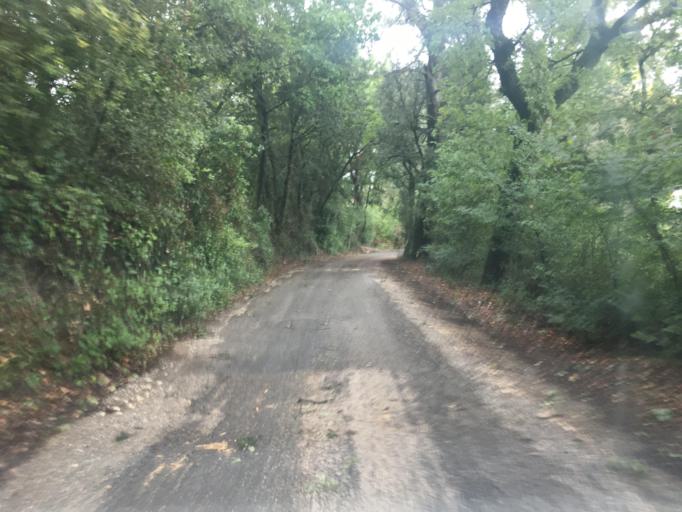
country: FR
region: Languedoc-Roussillon
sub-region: Departement du Gard
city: Montaren-et-Saint-Mediers
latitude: 44.0000
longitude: 4.3853
